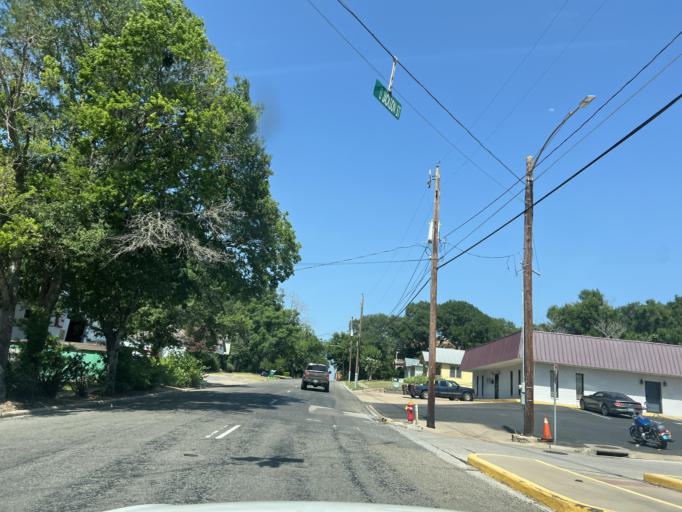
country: US
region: Texas
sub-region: Washington County
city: Brenham
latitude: 30.1652
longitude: -96.4049
